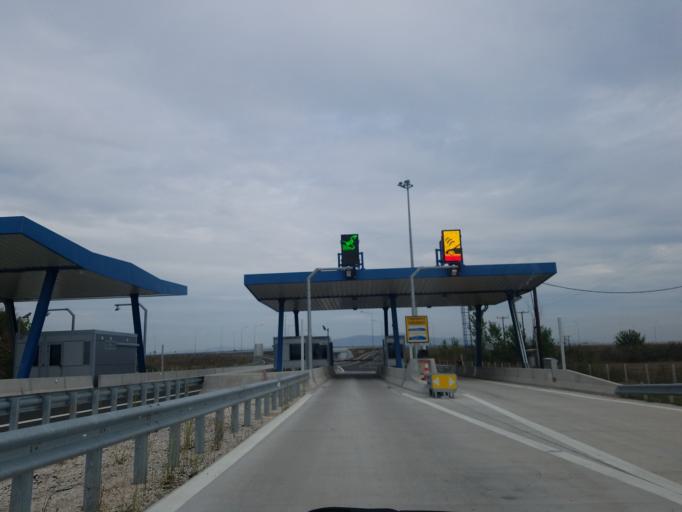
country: GR
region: Thessaly
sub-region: Nomos Kardhitsas
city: Agia Triada
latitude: 39.4743
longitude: 21.9032
